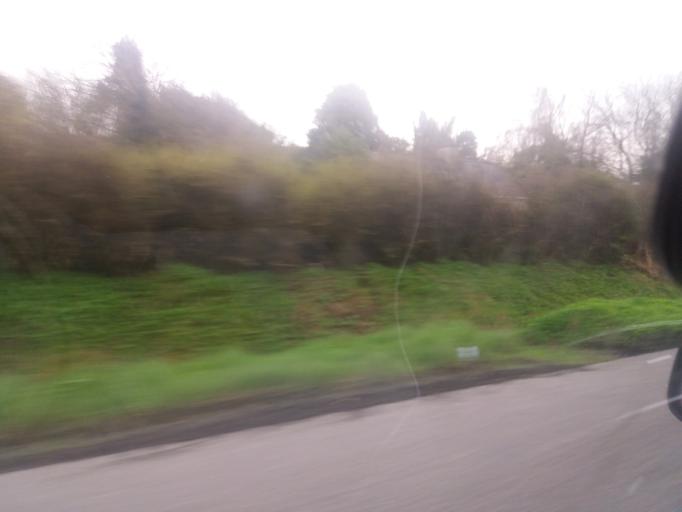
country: IE
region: Munster
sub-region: County Limerick
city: Newcastle West
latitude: 52.4187
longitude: -9.1452
